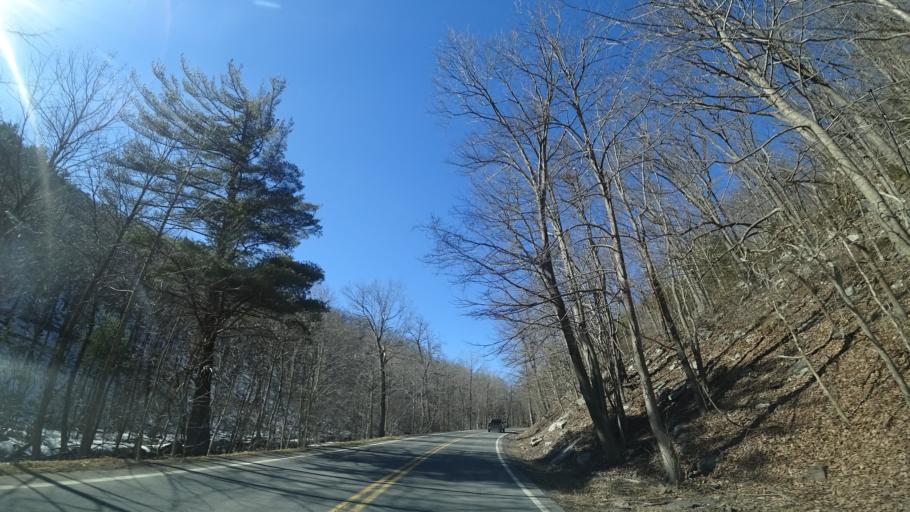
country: US
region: Virginia
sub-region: Shenandoah County
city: Strasburg
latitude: 39.0968
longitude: -78.4696
